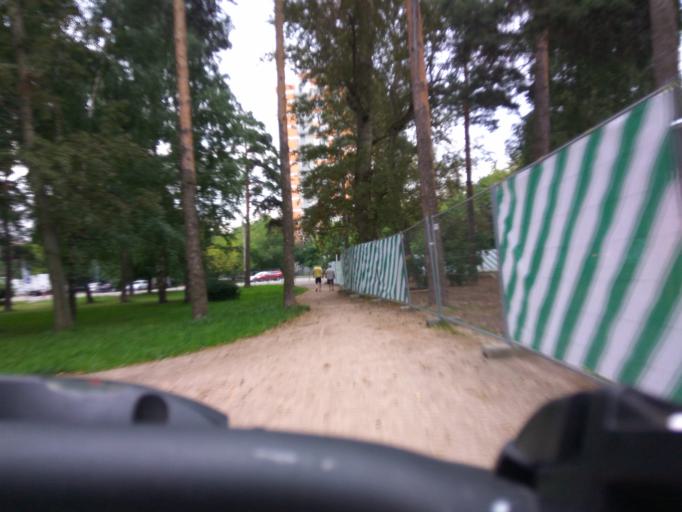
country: RU
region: Moscow
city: Tsaritsyno
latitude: 55.6265
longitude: 37.6596
